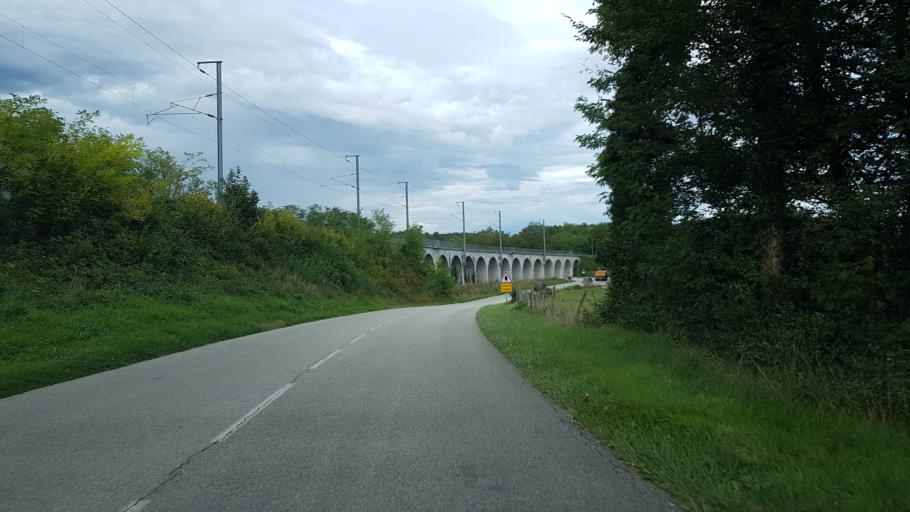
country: FR
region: Rhone-Alpes
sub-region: Departement de l'Ain
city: Villereversure
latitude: 46.1709
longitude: 5.3634
